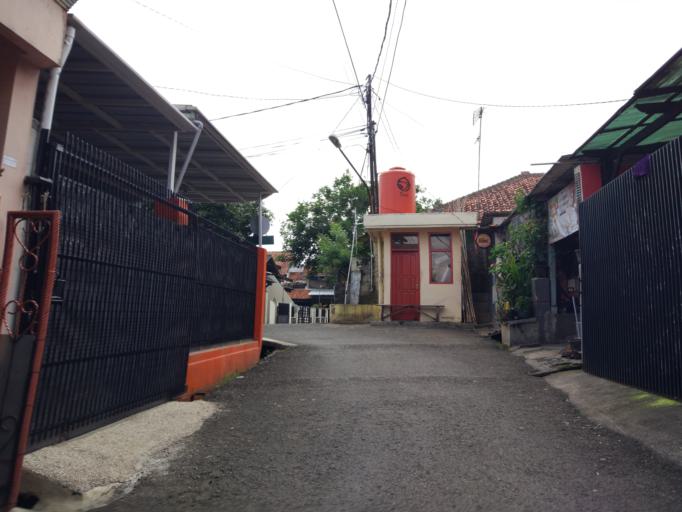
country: ID
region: West Java
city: Bandung
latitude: -6.9038
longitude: 107.6884
